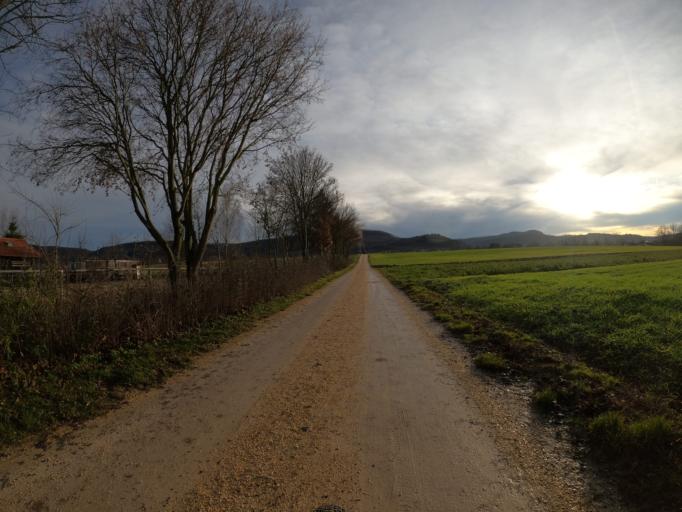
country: DE
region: Baden-Wuerttemberg
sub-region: Regierungsbezirk Stuttgart
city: Durnau
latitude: 48.6493
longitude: 9.6252
